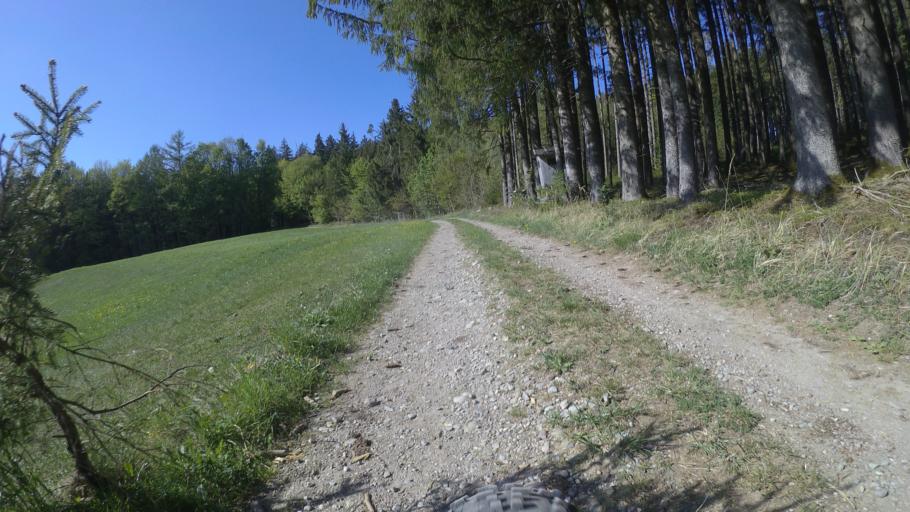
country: DE
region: Bavaria
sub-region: Upper Bavaria
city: Chieming
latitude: 47.9461
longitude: 12.5360
